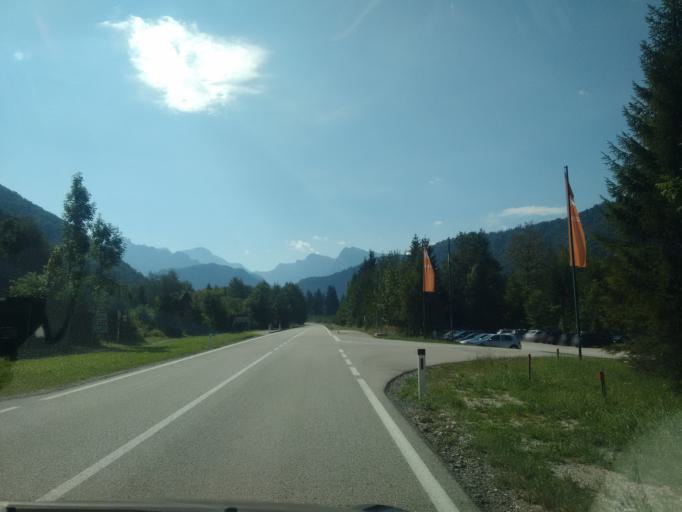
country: AT
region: Upper Austria
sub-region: Politischer Bezirk Gmunden
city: Gruenau im Almtal
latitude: 47.8073
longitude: 13.9513
